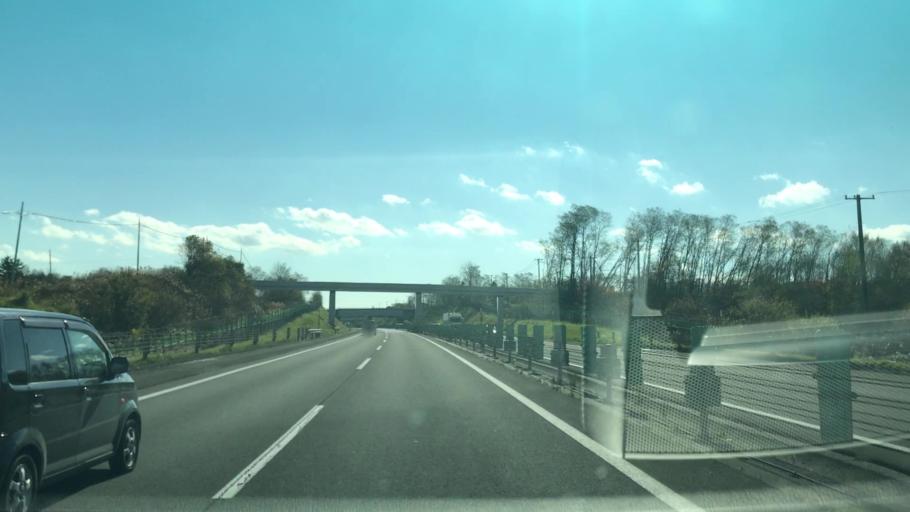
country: JP
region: Hokkaido
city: Kitahiroshima
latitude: 42.8895
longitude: 141.5492
